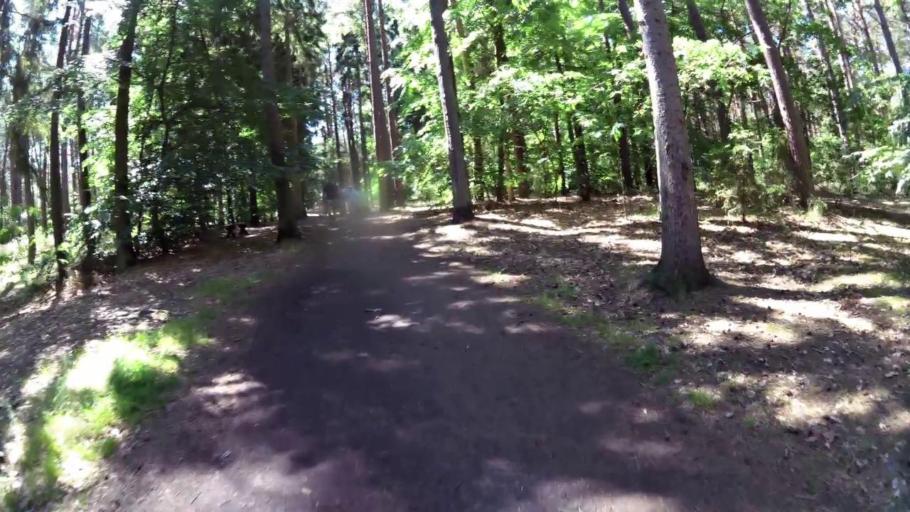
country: PL
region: West Pomeranian Voivodeship
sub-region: Powiat gryficki
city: Pobierowo
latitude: 54.0484
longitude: 14.8722
